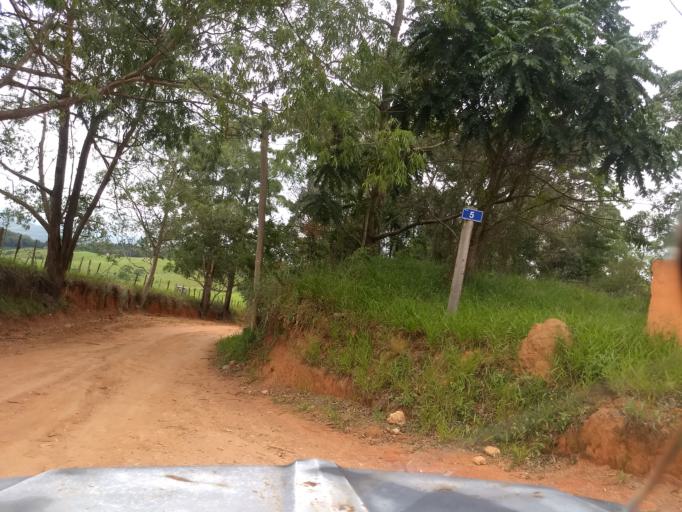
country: BR
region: Sao Paulo
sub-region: Cabreuva
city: Cabreuva
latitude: -23.3825
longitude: -47.1757
